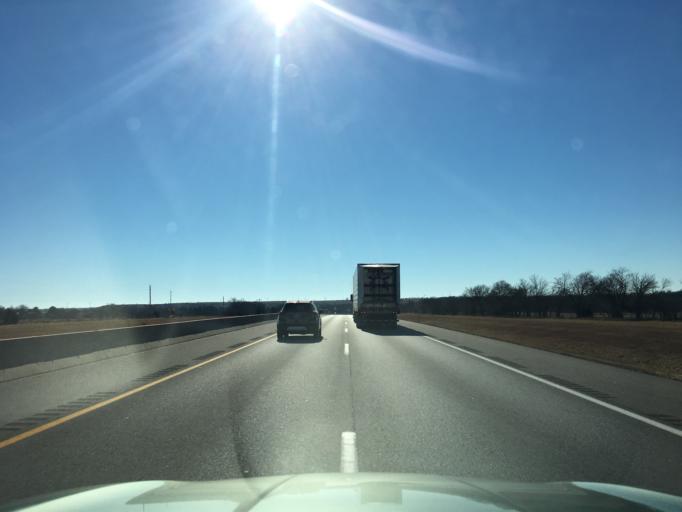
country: US
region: Kansas
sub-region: Sumner County
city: Wellington
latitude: 37.2243
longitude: -97.3389
